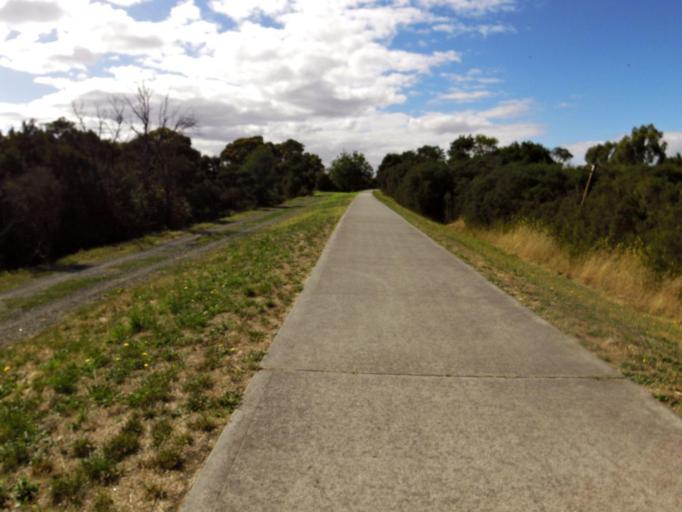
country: AU
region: Victoria
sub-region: Cardinia
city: Koo-Wee-Rup
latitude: -38.2008
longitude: 145.4920
